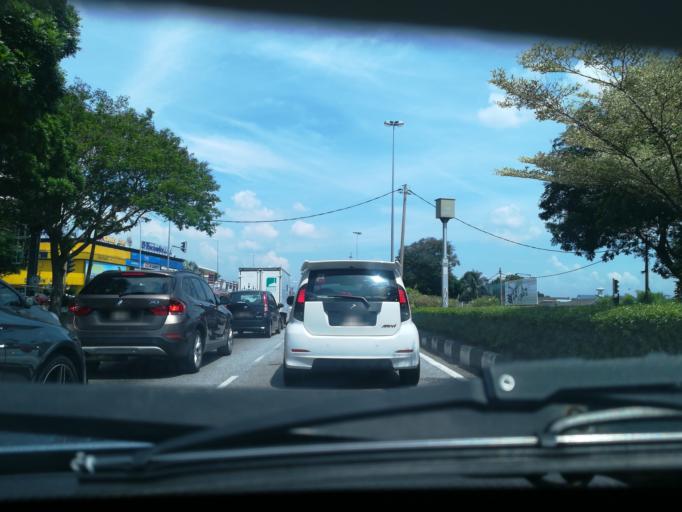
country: MY
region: Perak
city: Ipoh
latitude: 4.6129
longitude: 101.1174
